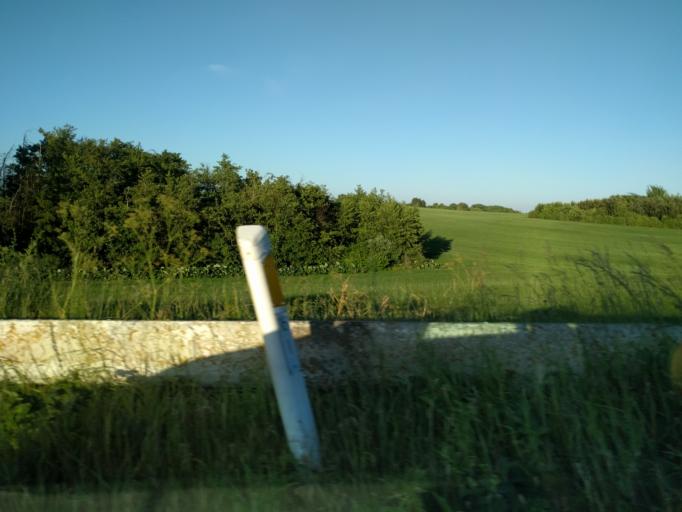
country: DK
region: South Denmark
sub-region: Kerteminde Kommune
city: Kerteminde
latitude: 55.5694
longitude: 10.6471
